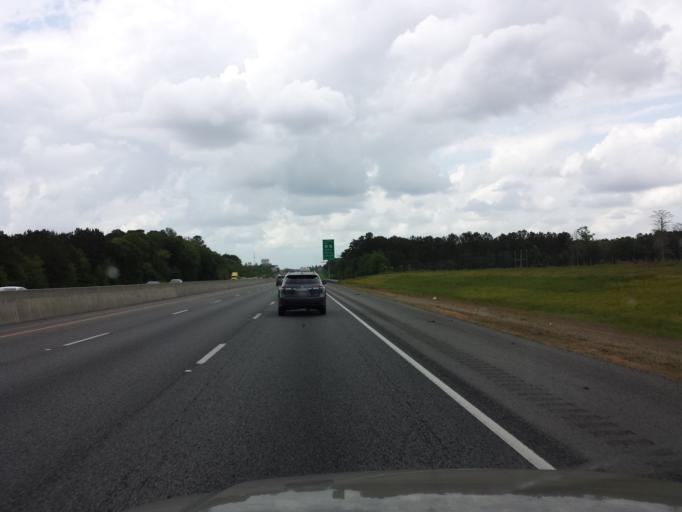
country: US
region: Georgia
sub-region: Lowndes County
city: Hahira
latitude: 30.9744
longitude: -83.3824
